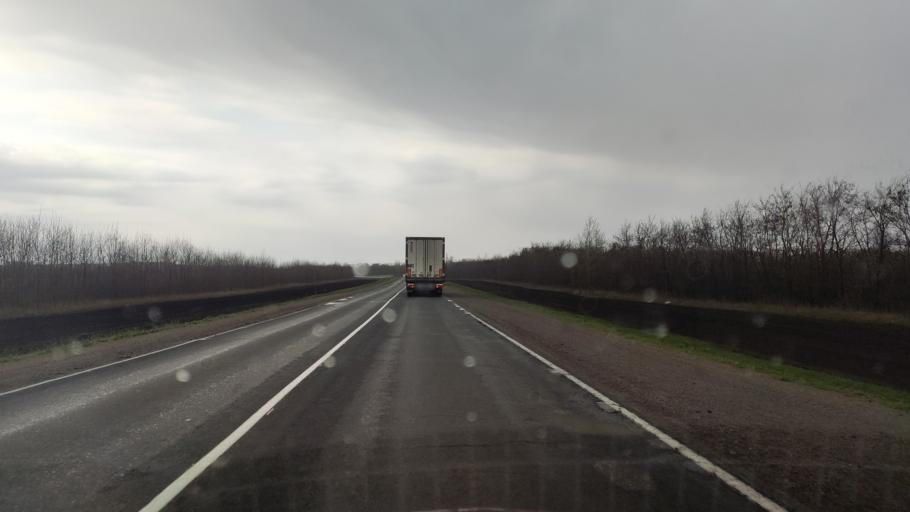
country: RU
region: Voronezj
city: Nizhnedevitsk
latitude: 51.5715
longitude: 38.3328
